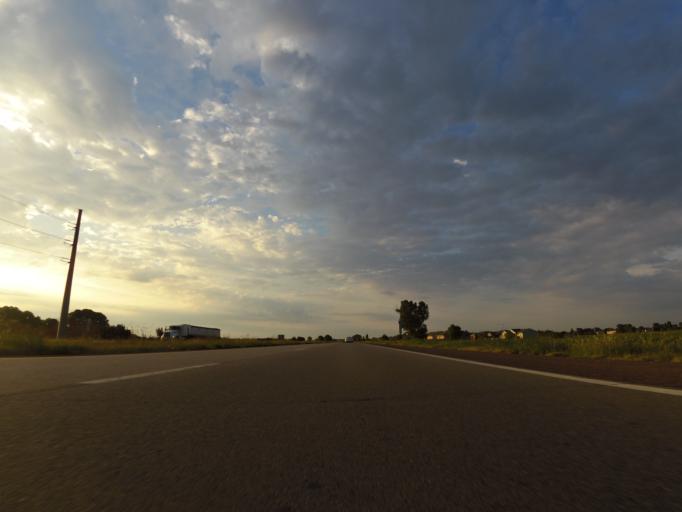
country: US
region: Kansas
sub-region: Sedgwick County
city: Maize
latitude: 37.7739
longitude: -97.4556
